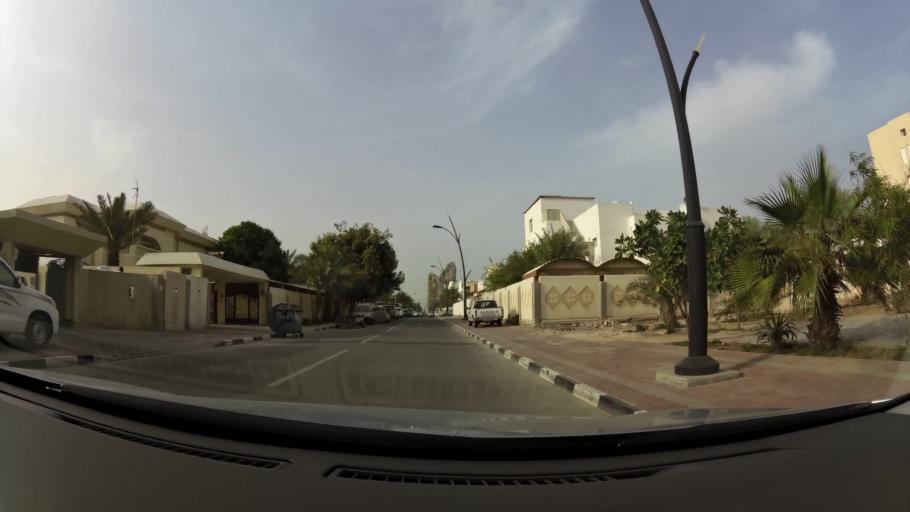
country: QA
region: Baladiyat ad Dawhah
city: Doha
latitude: 25.3277
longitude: 51.5176
